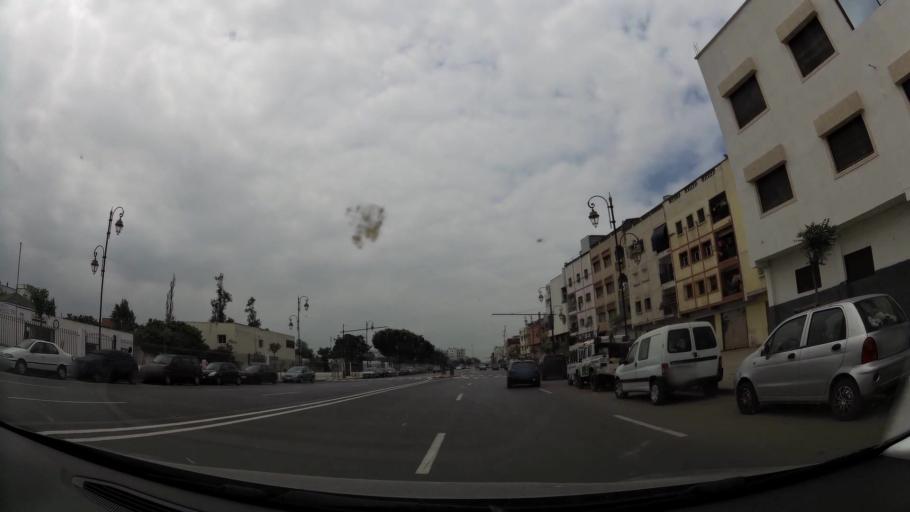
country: MA
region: Rabat-Sale-Zemmour-Zaer
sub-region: Skhirate-Temara
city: Temara
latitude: 33.9767
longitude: -6.8811
